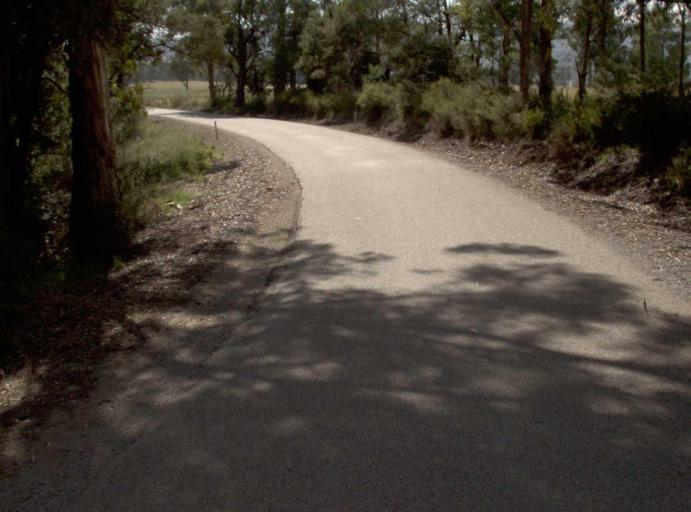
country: AU
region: Victoria
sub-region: East Gippsland
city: Lakes Entrance
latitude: -37.5246
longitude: 148.1417
